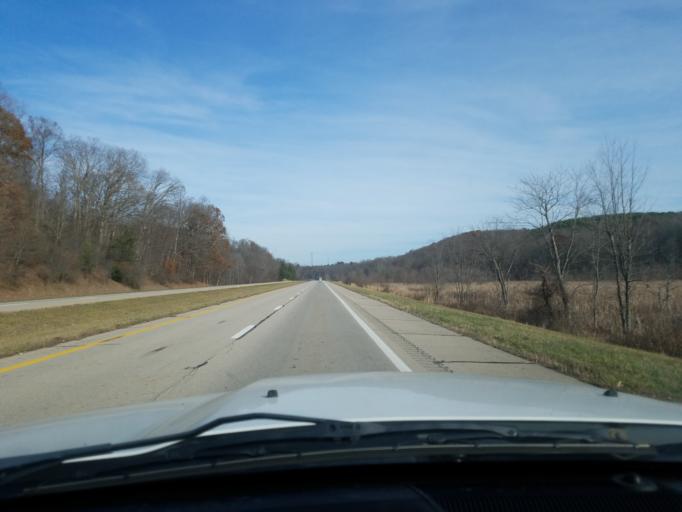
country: US
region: Ohio
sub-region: Jackson County
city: Wellston
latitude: 39.1014
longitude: -82.4832
